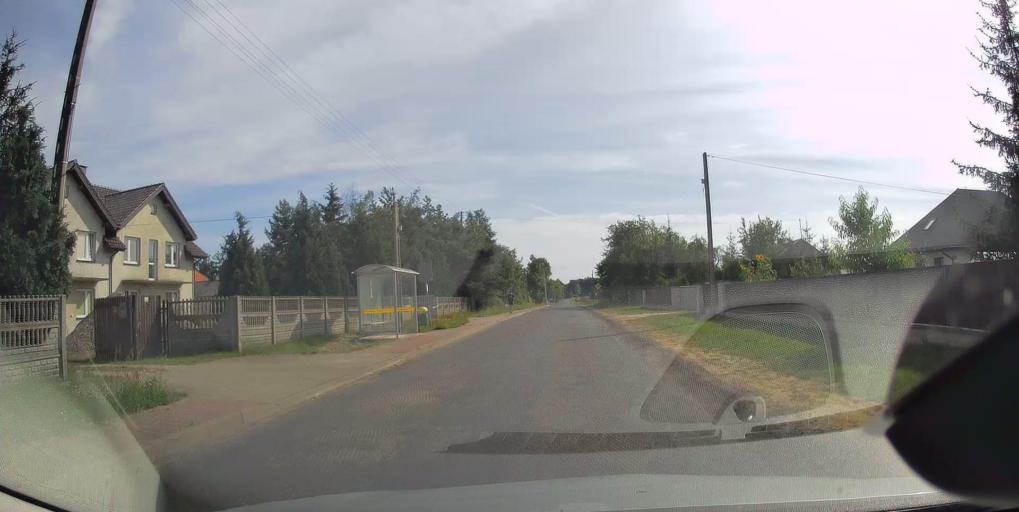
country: PL
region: Lodz Voivodeship
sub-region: Powiat opoczynski
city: Mniszkow
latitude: 51.4474
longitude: 20.0299
